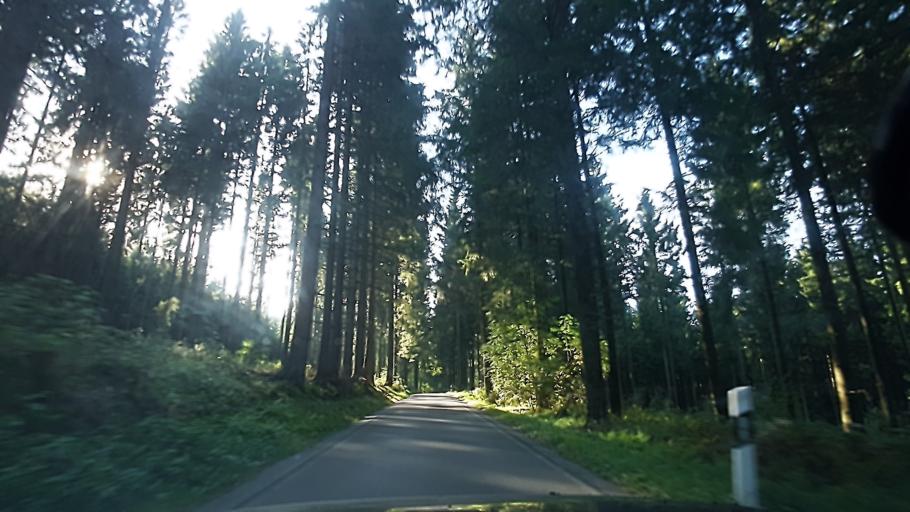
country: DE
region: North Rhine-Westphalia
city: Kierspe
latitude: 51.1461
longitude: 7.5560
